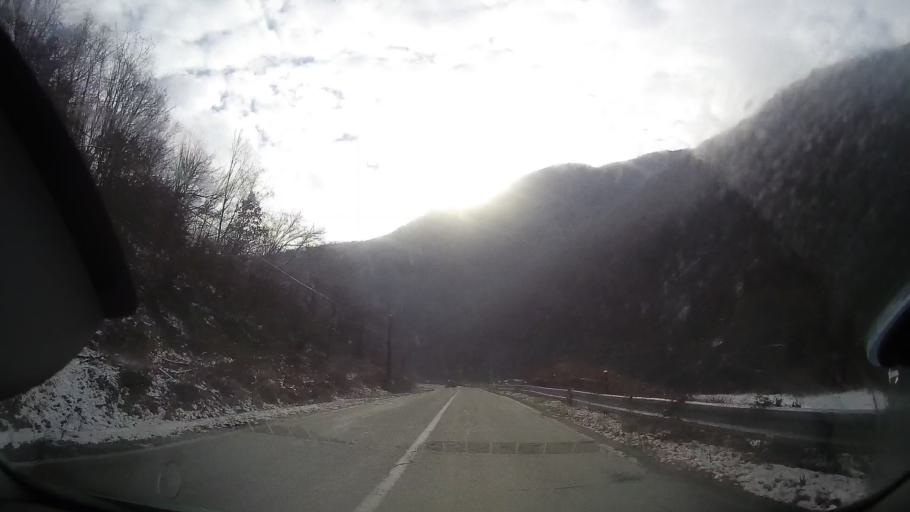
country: RO
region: Alba
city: Salciua de Sus
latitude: 46.4015
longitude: 23.3636
